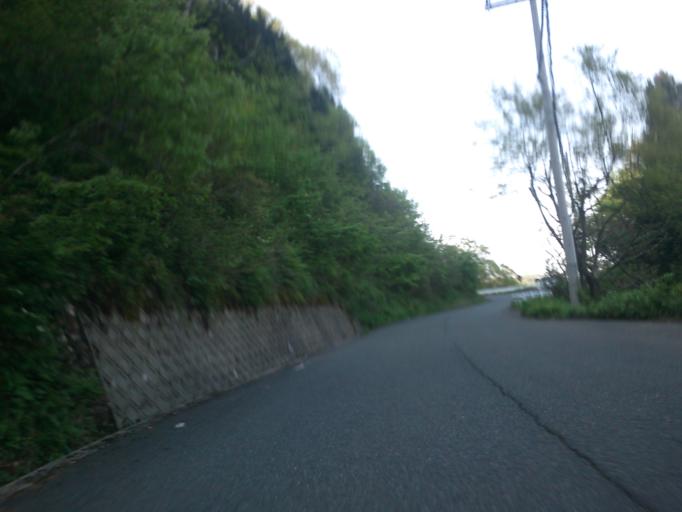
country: JP
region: Kyoto
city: Miyazu
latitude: 35.7113
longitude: 135.1941
